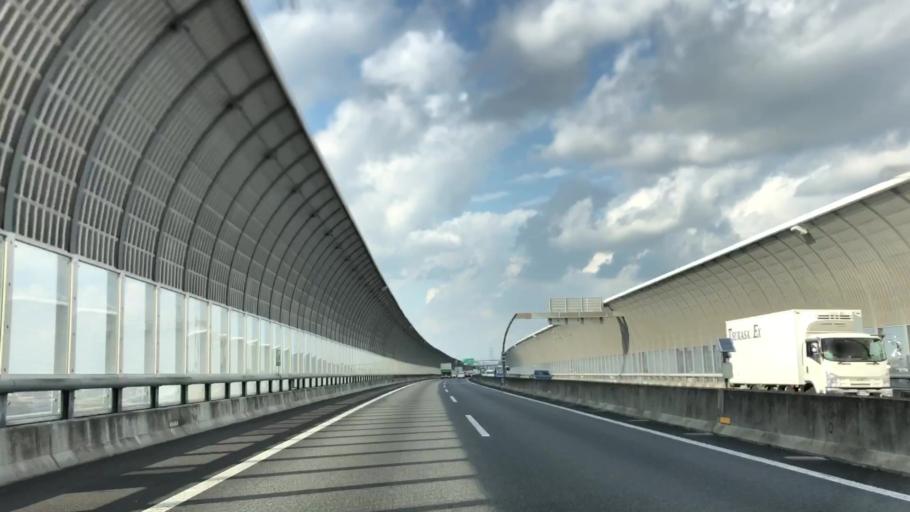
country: JP
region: Chiba
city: Matsudo
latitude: 35.8074
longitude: 139.8763
